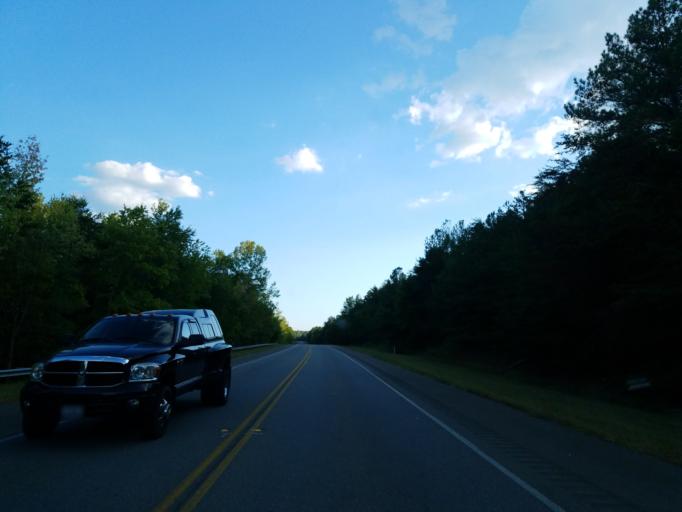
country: US
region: Georgia
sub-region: Murray County
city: Chatsworth
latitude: 34.6132
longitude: -84.7137
